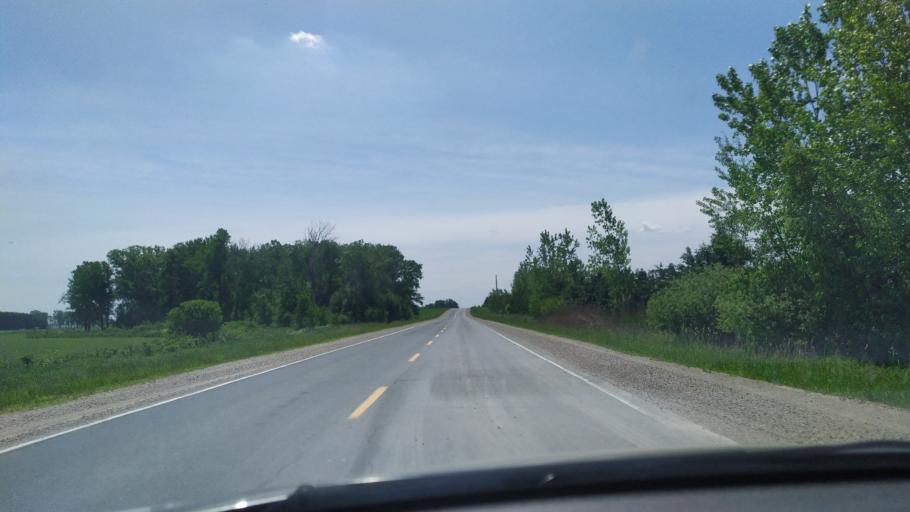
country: CA
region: Ontario
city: Ingersoll
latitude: 43.0419
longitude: -80.9789
